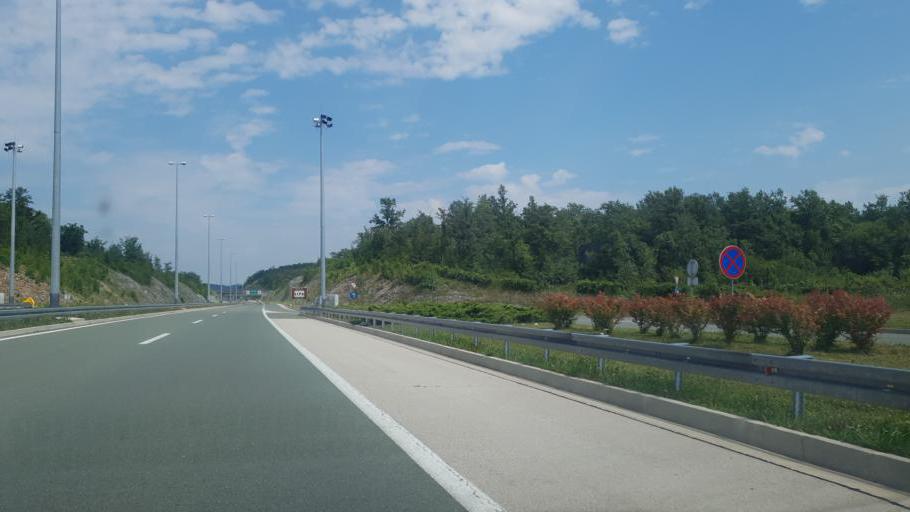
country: HR
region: Primorsko-Goranska
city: Matulji
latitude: 45.4437
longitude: 14.2740
